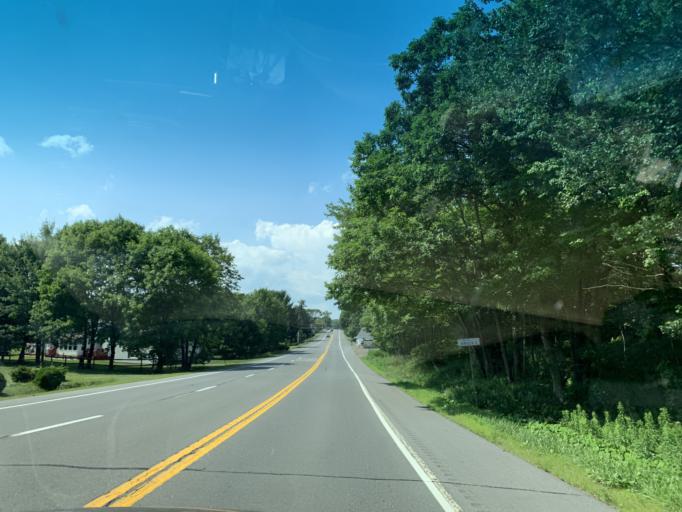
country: US
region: Pennsylvania
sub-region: Schuylkill County
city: Ashland
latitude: 40.8165
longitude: -76.3362
